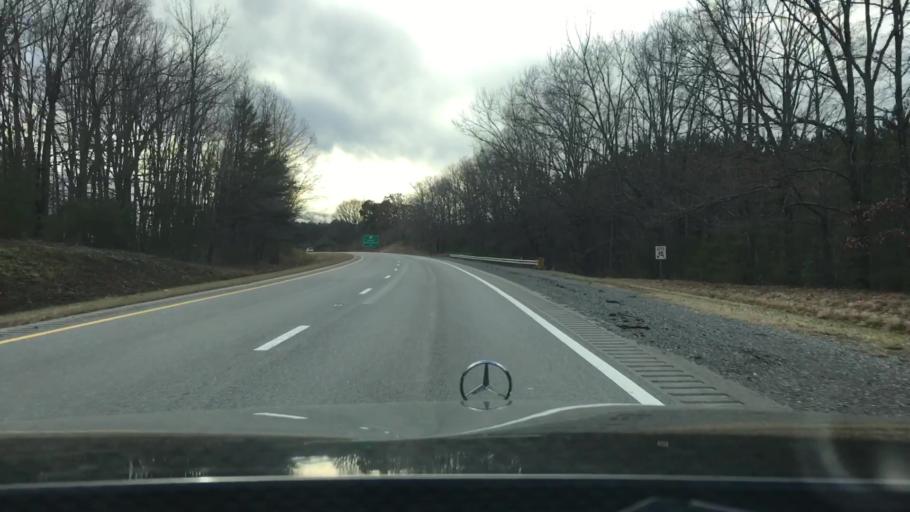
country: US
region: Virginia
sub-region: Pittsylvania County
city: Gretna
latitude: 36.9604
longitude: -79.3755
